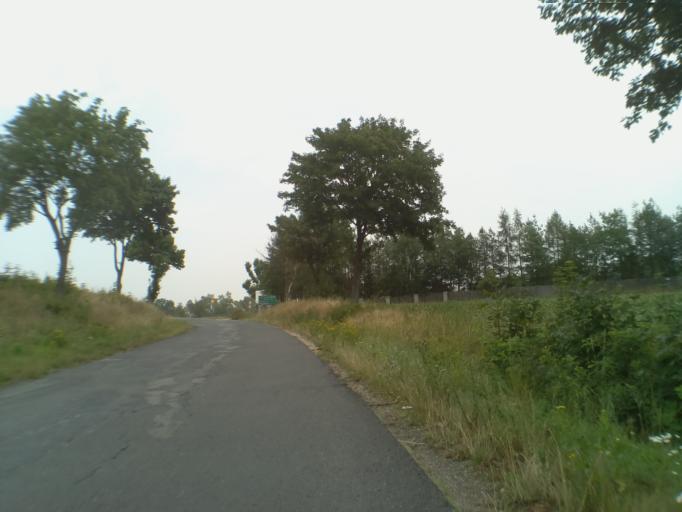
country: PL
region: Lower Silesian Voivodeship
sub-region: Powiat swidnicki
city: Strzegom
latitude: 50.9427
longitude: 16.3306
